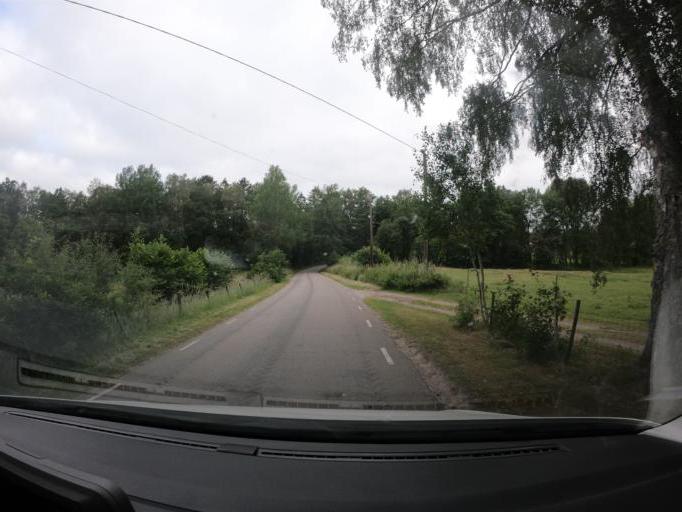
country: SE
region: Skane
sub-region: Klippans Kommun
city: Ljungbyhed
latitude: 56.0533
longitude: 13.2540
